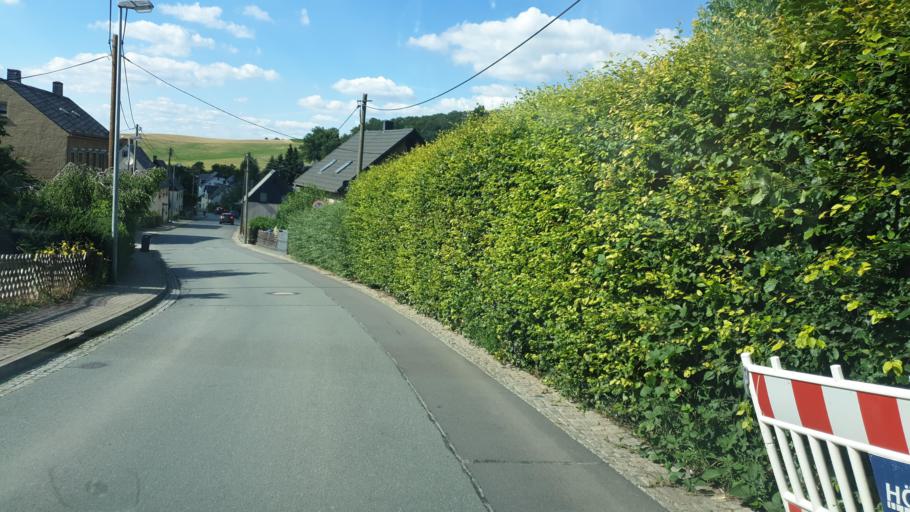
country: DE
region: Saxony
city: Burkhardtsdorf
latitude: 50.7515
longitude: 12.9254
